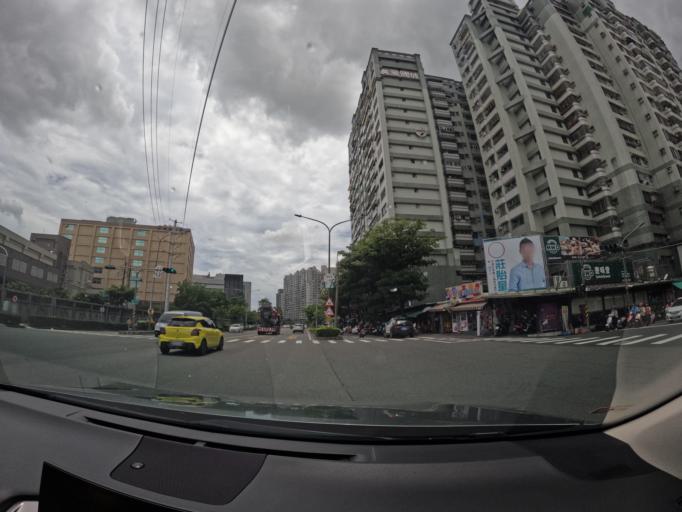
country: TW
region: Kaohsiung
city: Kaohsiung
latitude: 22.7255
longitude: 120.3046
